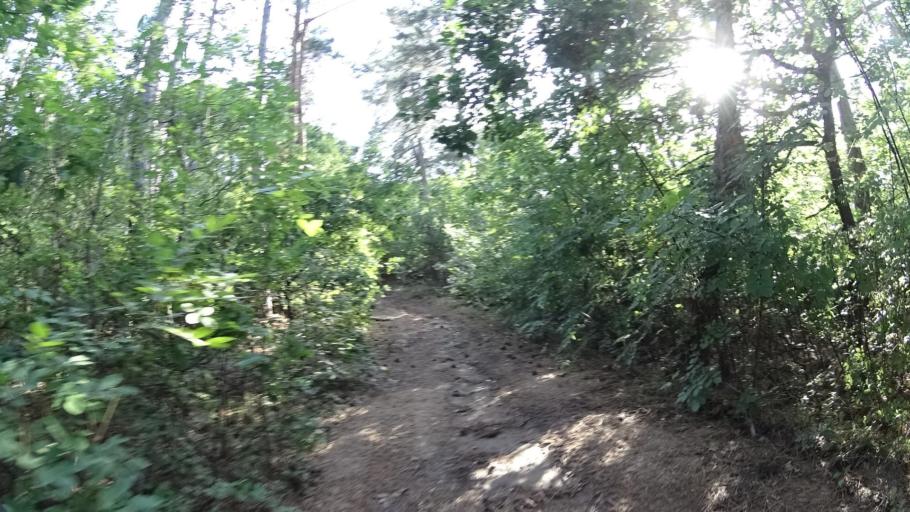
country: BG
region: Plovdiv
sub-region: Obshtina Plovdiv
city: Plovdiv
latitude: 42.0566
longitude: 24.6864
